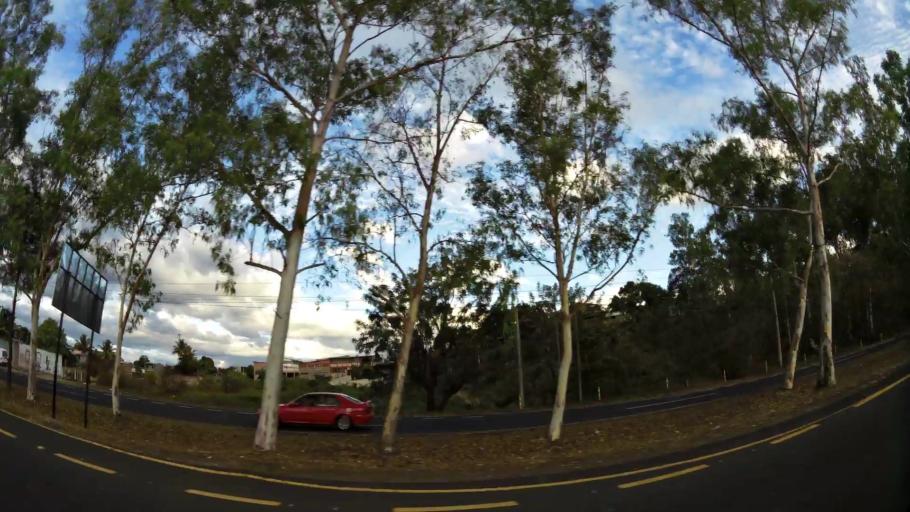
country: SV
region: San Vicente
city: San Sebastian
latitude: 13.7171
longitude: -88.8583
